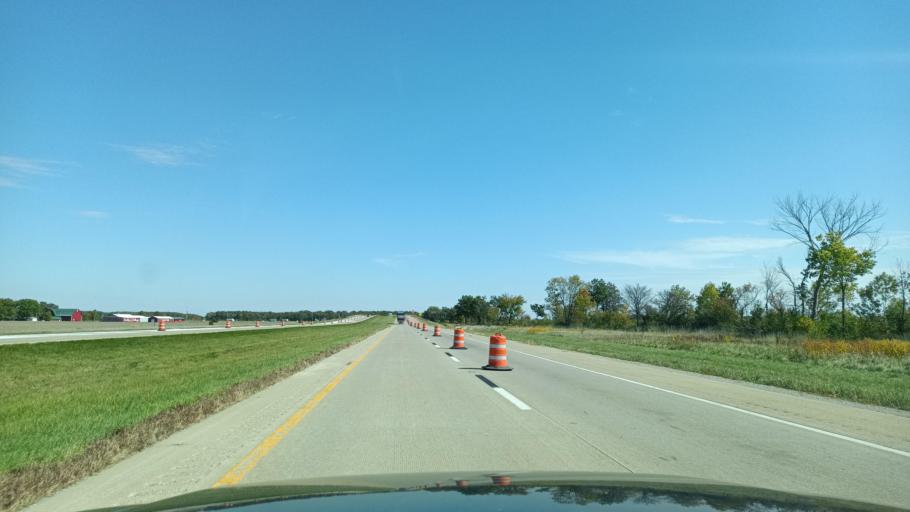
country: US
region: Ohio
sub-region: Defiance County
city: Defiance
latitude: 41.2595
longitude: -84.4456
